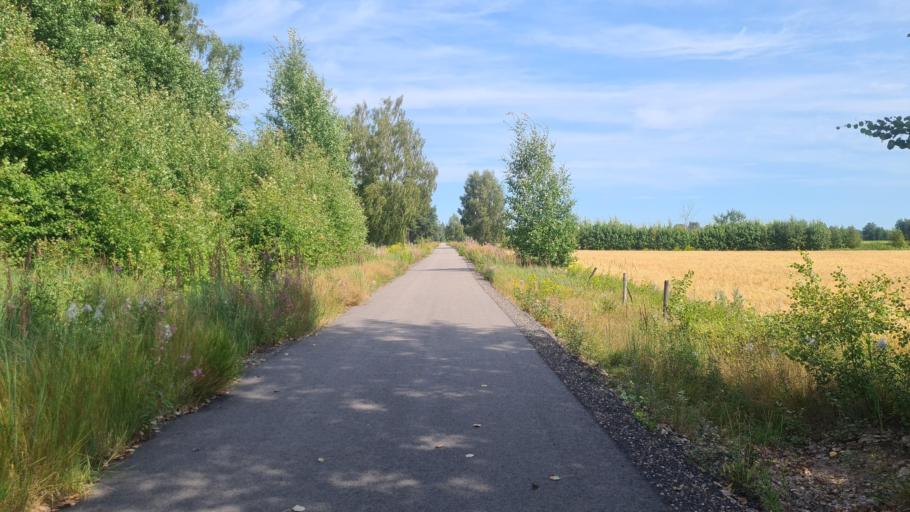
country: SE
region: Kronoberg
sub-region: Ljungby Kommun
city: Lagan
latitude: 56.8988
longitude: 13.9888
